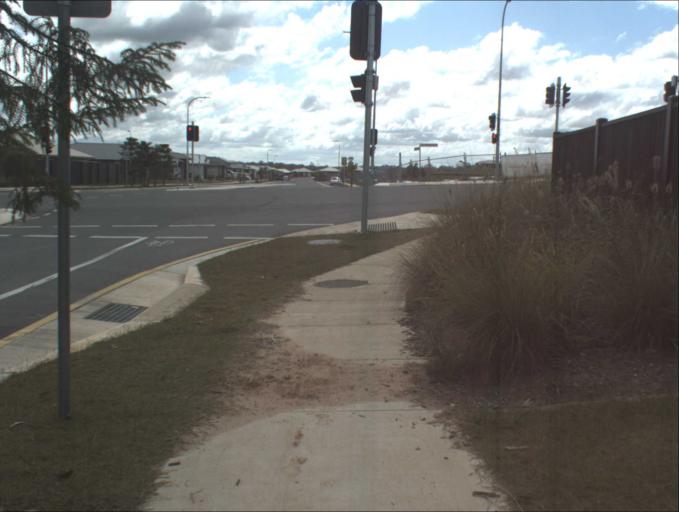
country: AU
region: Queensland
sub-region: Logan
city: Chambers Flat
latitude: -27.8052
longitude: 153.1116
